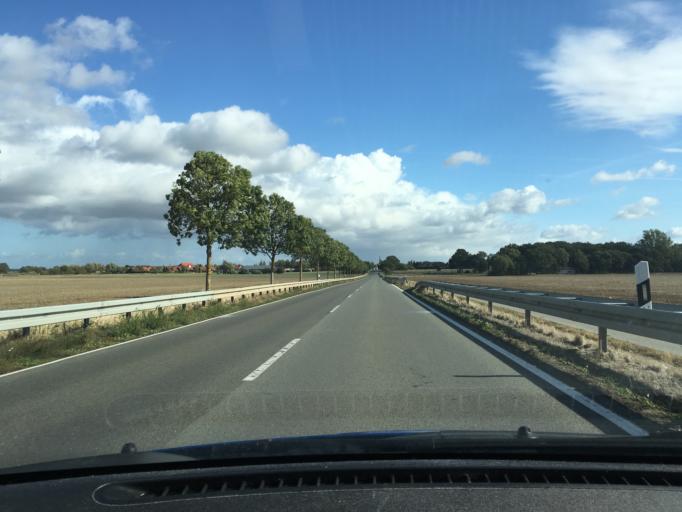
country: DE
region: Saxony-Anhalt
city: Pretzier
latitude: 52.8362
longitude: 11.2442
